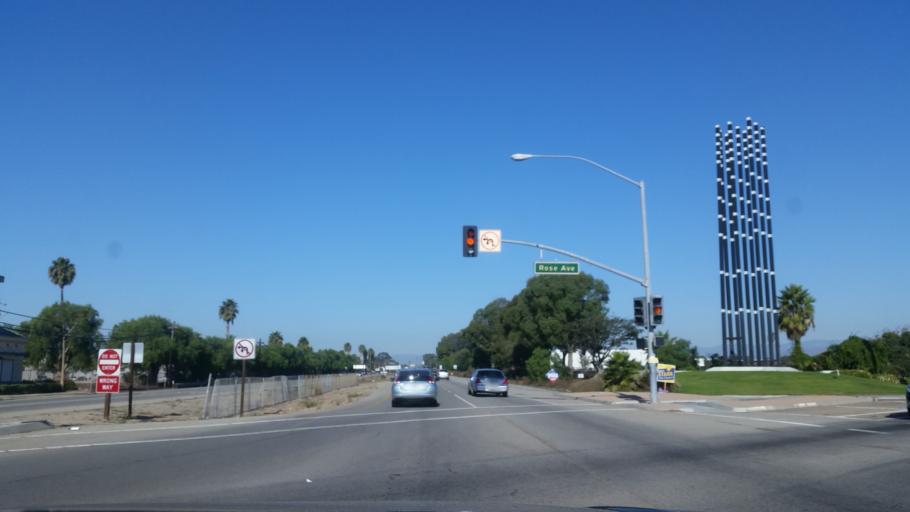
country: US
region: California
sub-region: Ventura County
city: Oxnard
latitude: 34.1755
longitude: -119.1600
